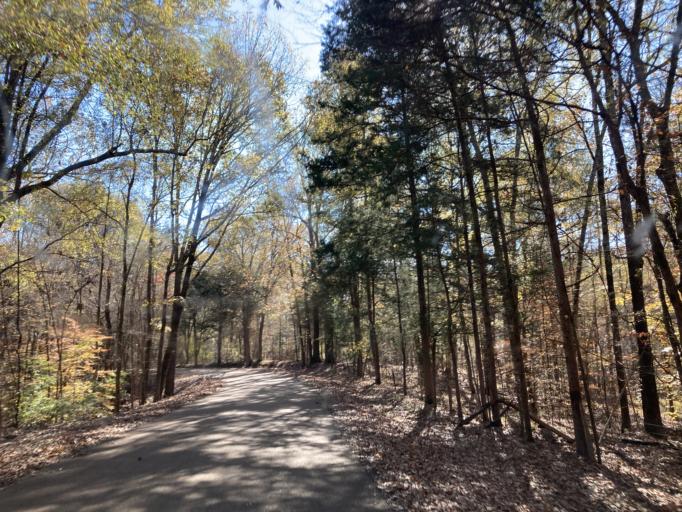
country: US
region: Mississippi
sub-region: Hinds County
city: Lynchburg
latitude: 32.5892
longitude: -90.5192
